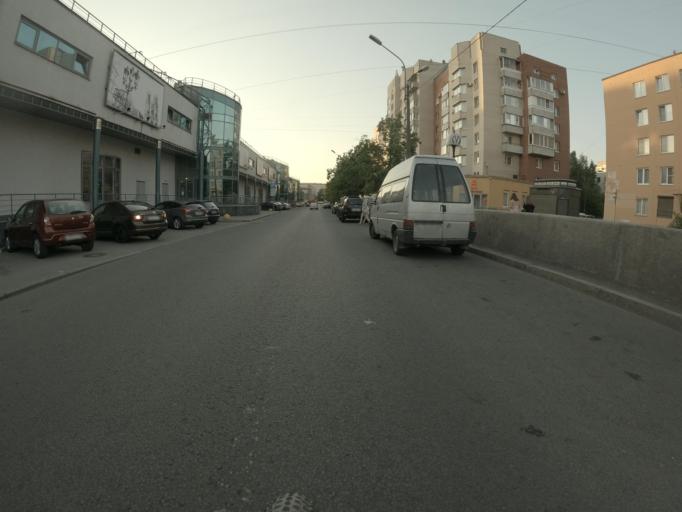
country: RU
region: St.-Petersburg
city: Dachnoye
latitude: 59.8498
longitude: 30.2689
